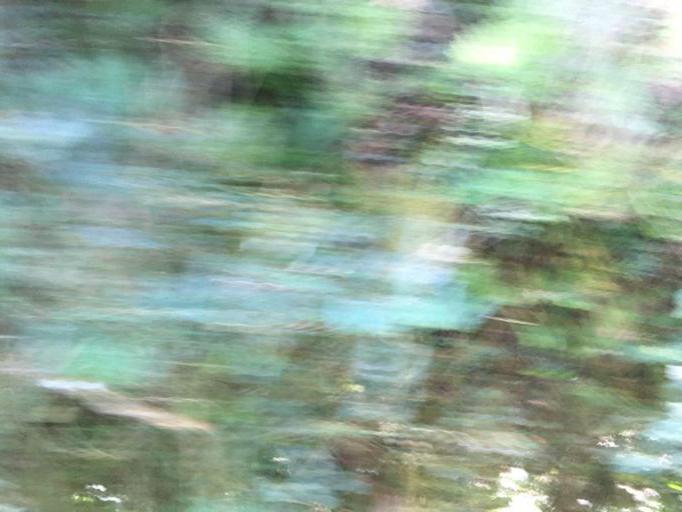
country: TW
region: Taiwan
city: Daxi
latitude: 24.5790
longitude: 121.4117
